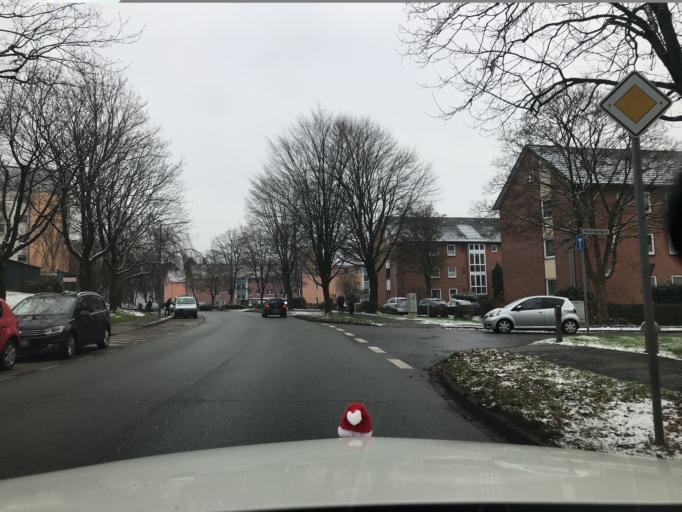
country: DE
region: Schleswig-Holstein
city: Flensburg
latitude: 54.7813
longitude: 9.4156
